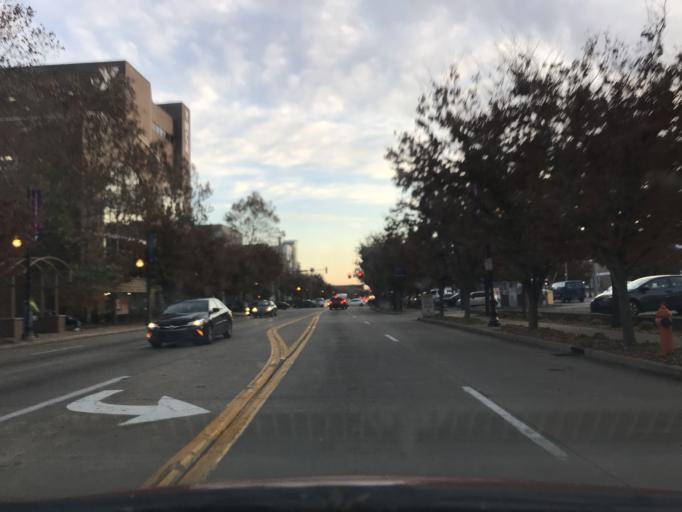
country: US
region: Kentucky
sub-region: Jefferson County
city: Louisville
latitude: 38.2495
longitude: -85.7545
